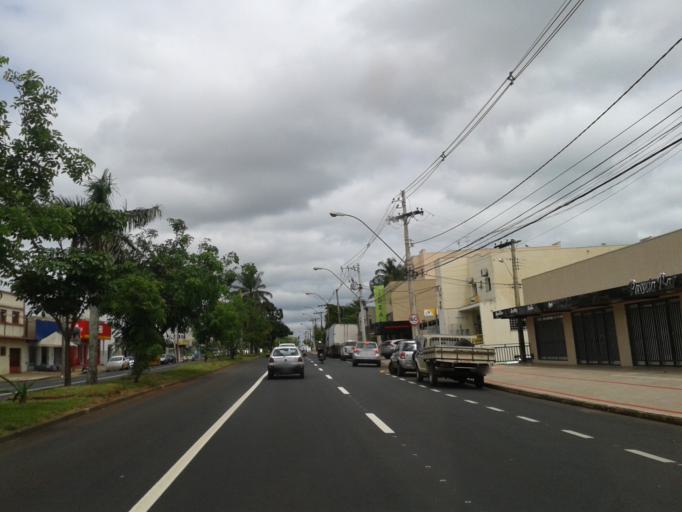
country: BR
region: Minas Gerais
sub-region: Uberaba
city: Uberaba
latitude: -19.7433
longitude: -47.9570
